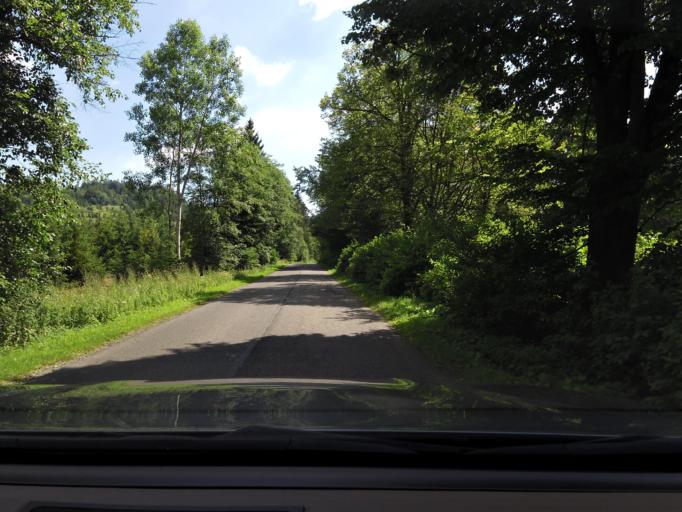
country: PL
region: Silesian Voivodeship
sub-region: Powiat zywiecki
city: Laliki
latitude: 49.5258
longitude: 19.0118
